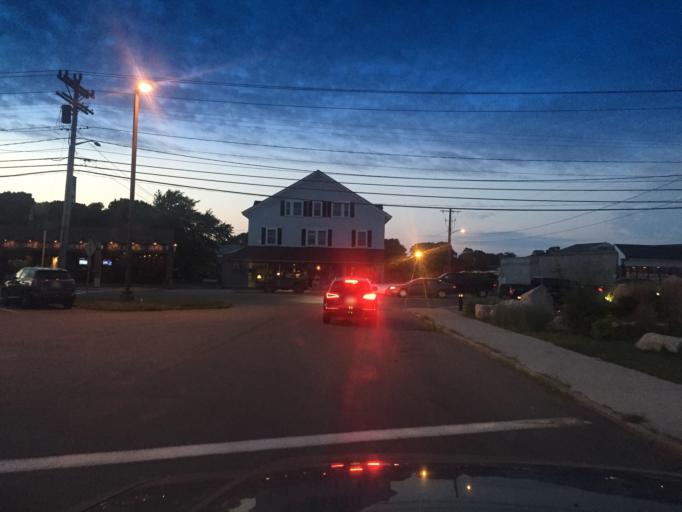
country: US
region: Massachusetts
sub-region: Barnstable County
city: Buzzards Bay
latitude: 41.7448
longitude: -70.6152
